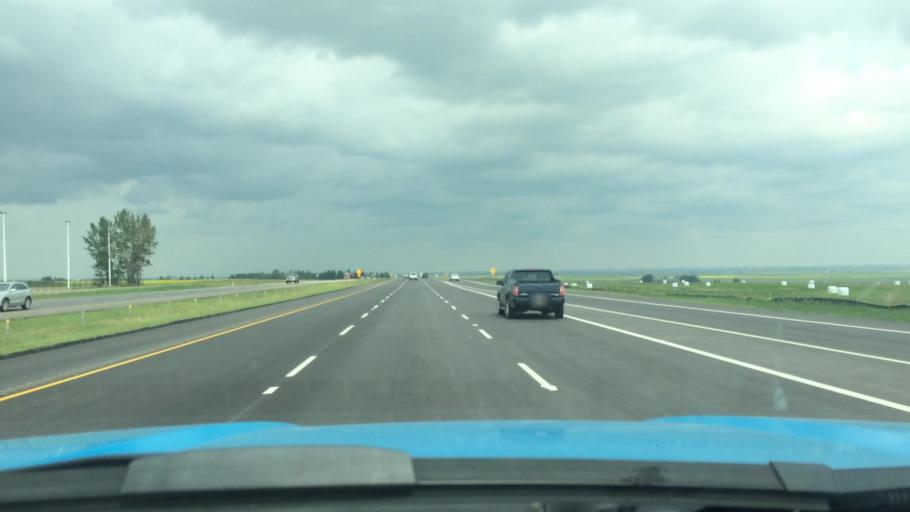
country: CA
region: Alberta
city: Crossfield
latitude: 51.4190
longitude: -114.0017
